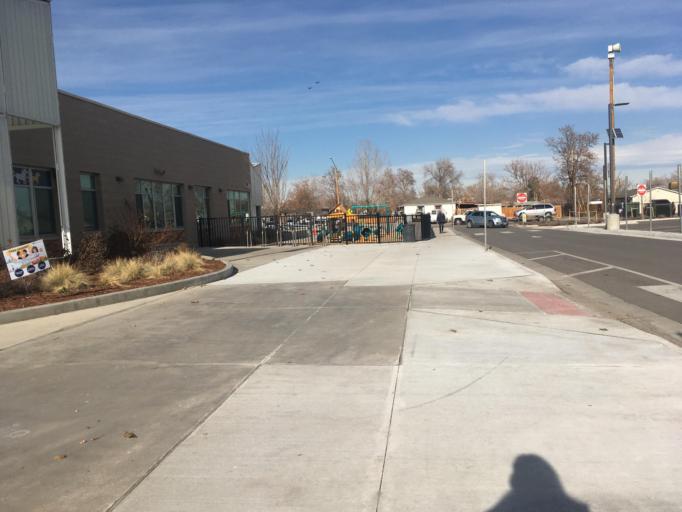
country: US
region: Colorado
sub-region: Adams County
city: Commerce City
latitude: 39.7813
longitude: -104.9558
